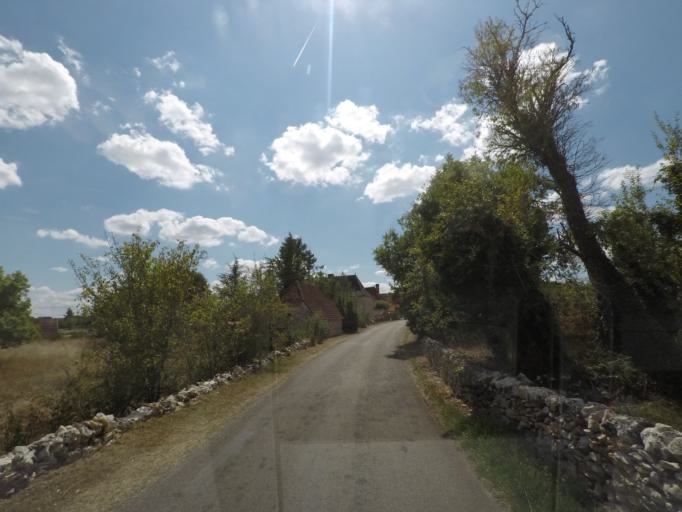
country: FR
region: Midi-Pyrenees
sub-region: Departement du Lot
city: Cajarc
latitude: 44.5465
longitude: 1.6687
